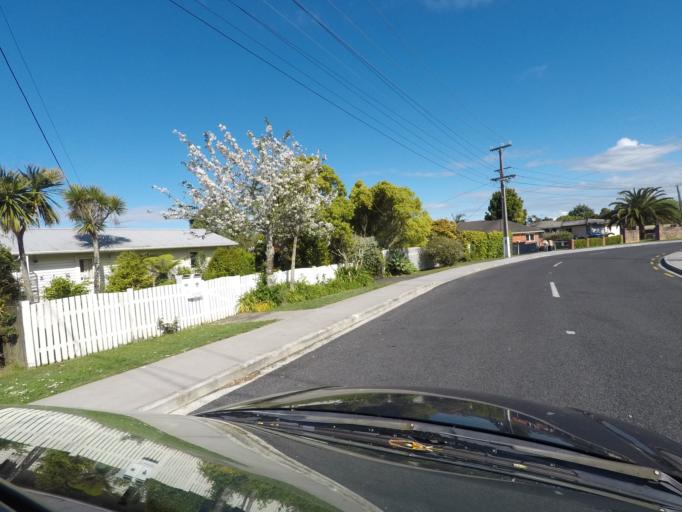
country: NZ
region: Auckland
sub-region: Auckland
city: Rosebank
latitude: -36.8638
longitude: 174.6525
